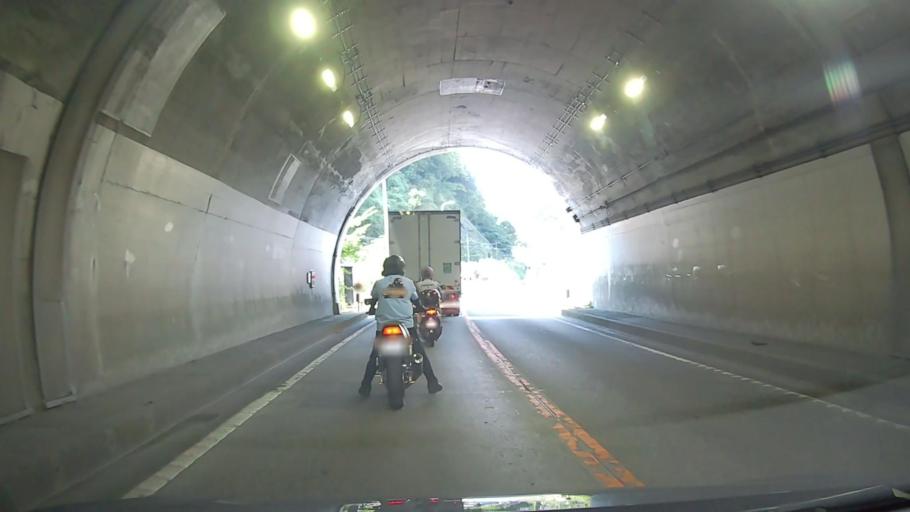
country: JP
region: Shizuoka
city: Gotemba
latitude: 35.3631
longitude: 139.0419
